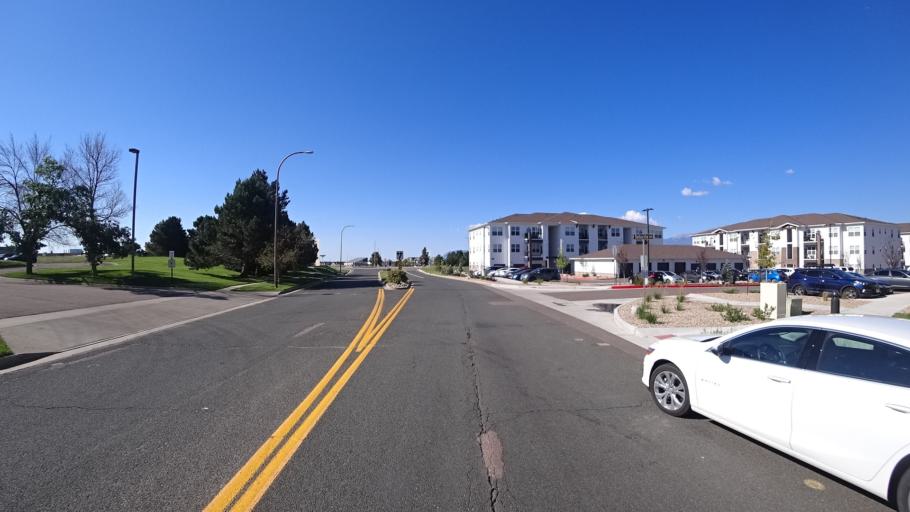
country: US
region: Colorado
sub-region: El Paso County
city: Gleneagle
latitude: 38.9957
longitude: -104.7934
